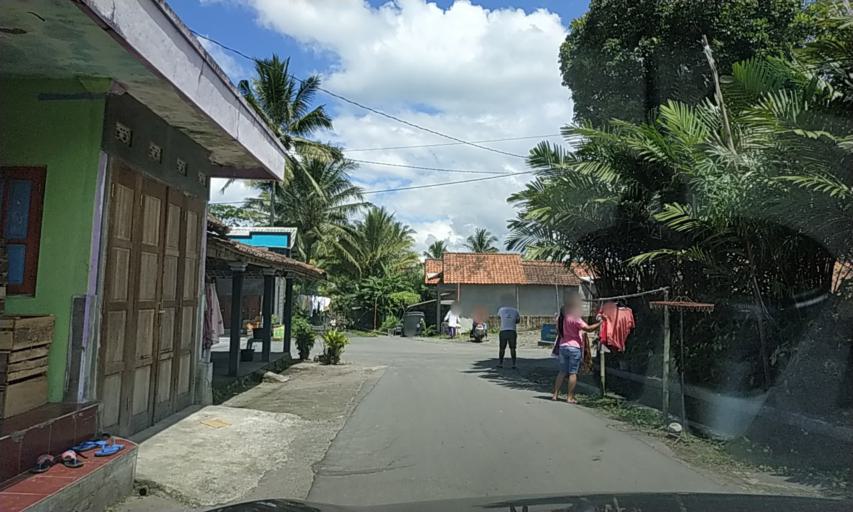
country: ID
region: Central Java
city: Muntilan
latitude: -7.5929
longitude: 110.3494
